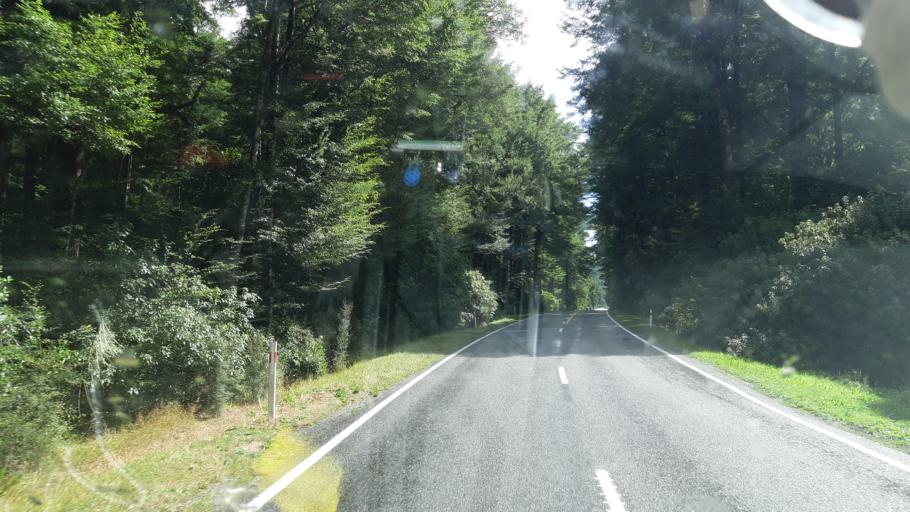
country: NZ
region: Canterbury
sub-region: Hurunui District
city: Amberley
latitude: -42.3820
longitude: 172.2999
